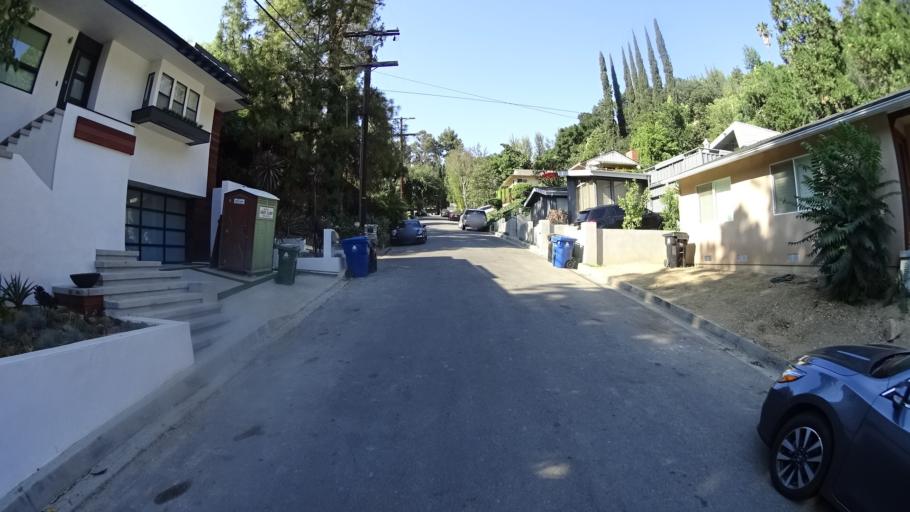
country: US
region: California
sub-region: Los Angeles County
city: Universal City
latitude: 34.1350
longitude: -118.3863
